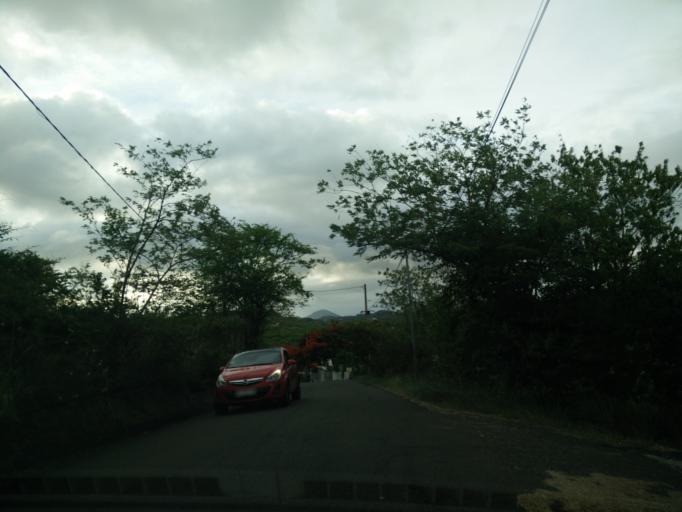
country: MQ
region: Martinique
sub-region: Martinique
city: Le Marin
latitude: 14.4524
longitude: -60.8403
